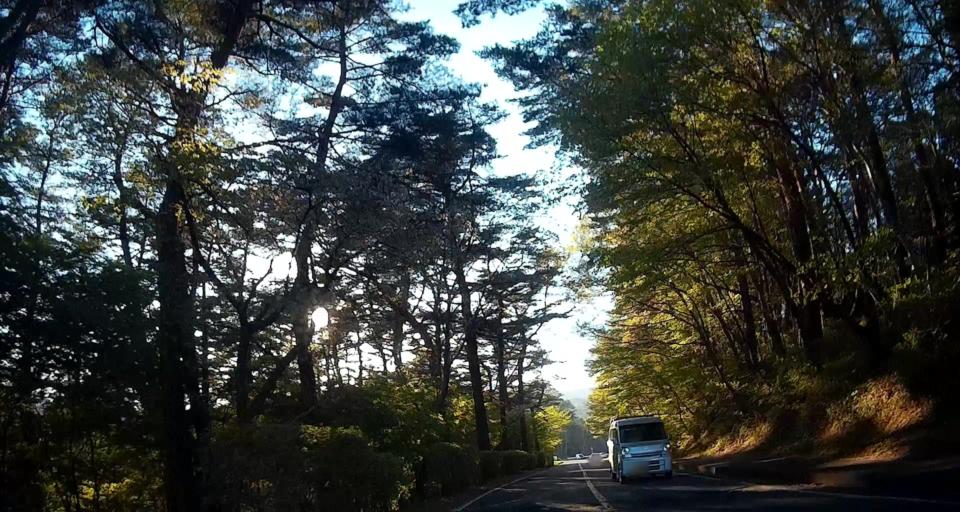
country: JP
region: Iwate
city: Miyako
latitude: 39.6491
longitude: 141.9759
